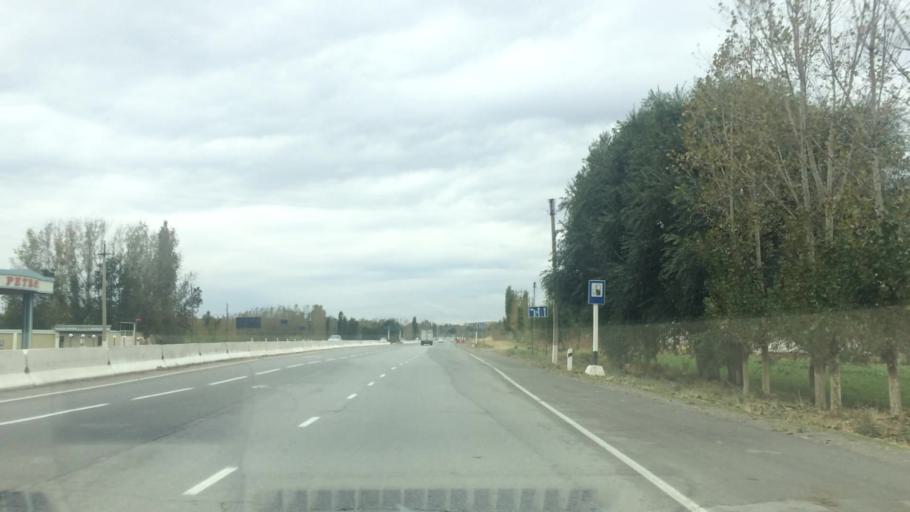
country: UZ
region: Jizzax
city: Jizzax
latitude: 39.9620
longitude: 67.5479
